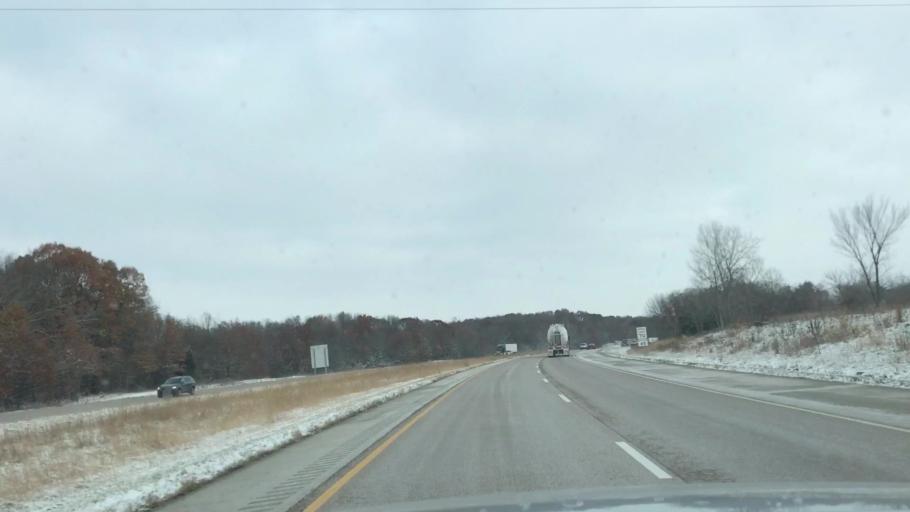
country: US
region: Illinois
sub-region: Macoupin County
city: Mount Olive
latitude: 39.0806
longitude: -89.7550
